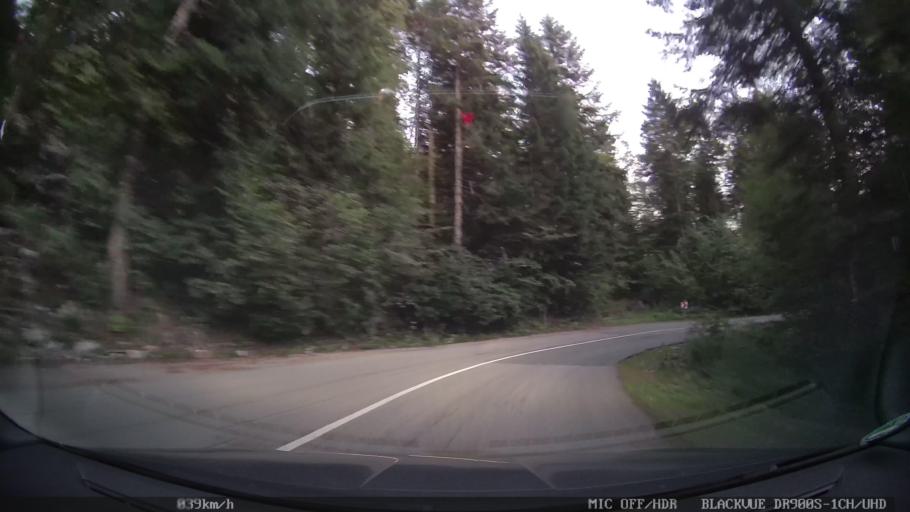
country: HR
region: Primorsko-Goranska
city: Novi Vinodolski
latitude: 45.1933
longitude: 14.8807
